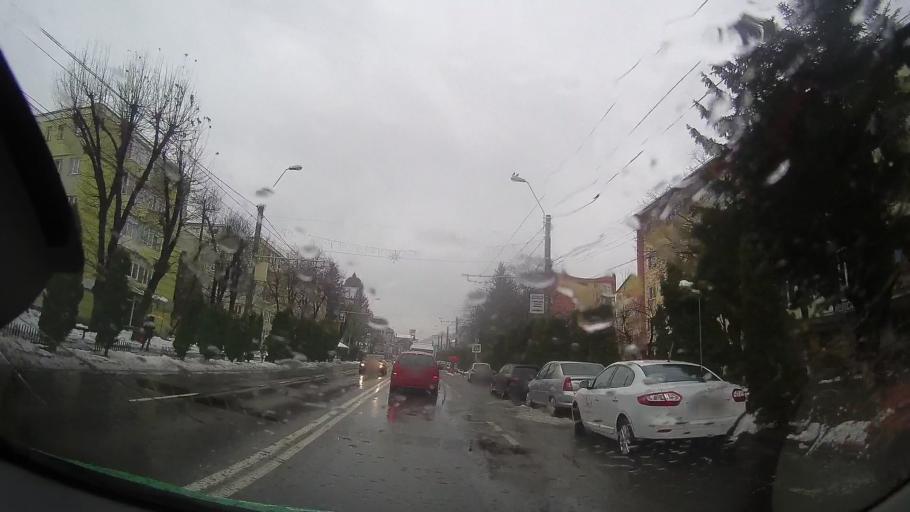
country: RO
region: Neamt
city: Piatra Neamt
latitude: 46.9350
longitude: 26.3551
